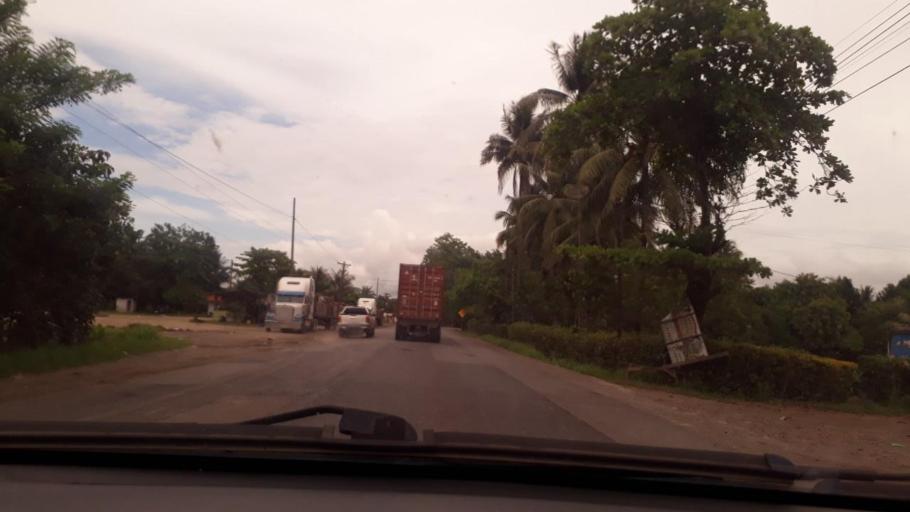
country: GT
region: Izabal
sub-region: Municipio de Puerto Barrios
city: Puerto Barrios
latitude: 15.5828
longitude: -88.5956
